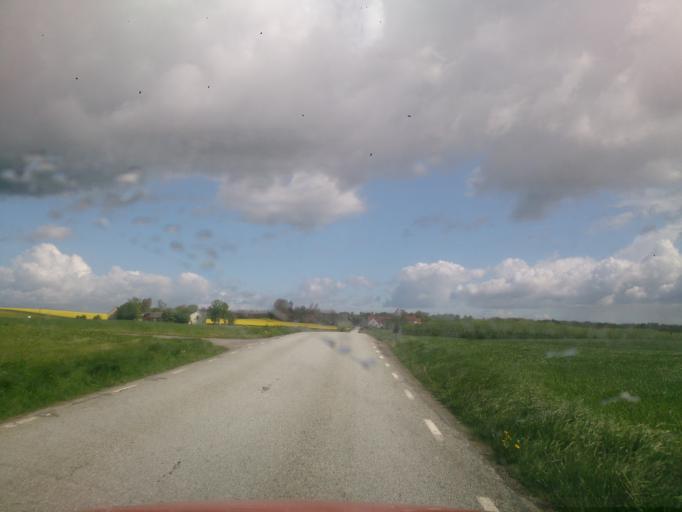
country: SE
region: Skane
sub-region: Ystads Kommun
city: Ystad
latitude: 55.4809
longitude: 13.7108
